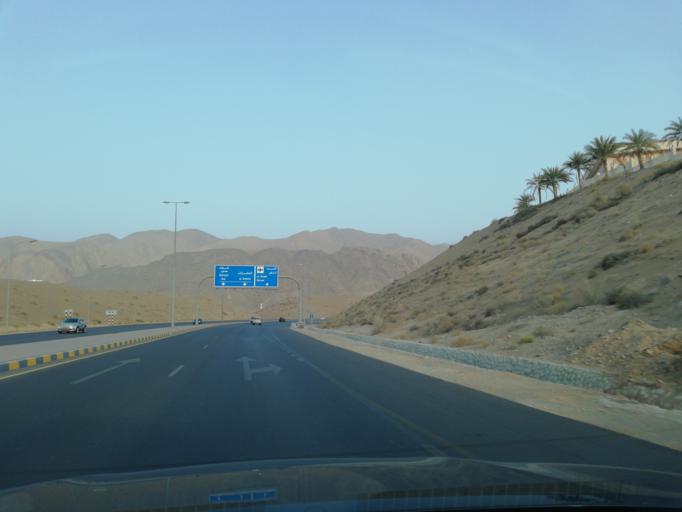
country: OM
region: Muhafazat Masqat
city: Bawshar
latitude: 23.5762
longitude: 58.4222
